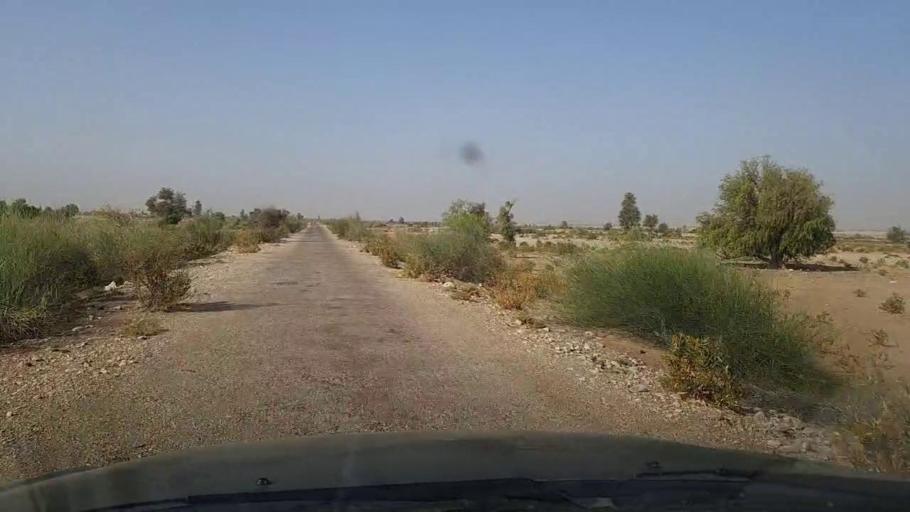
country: PK
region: Sindh
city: Sann
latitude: 25.9563
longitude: 68.0419
